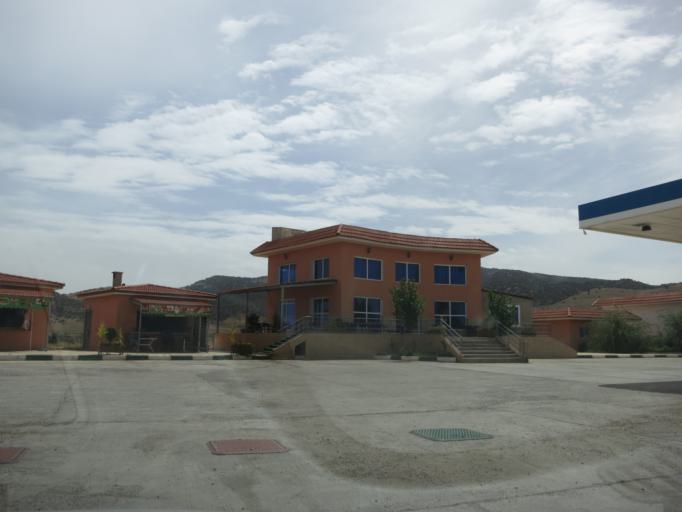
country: MA
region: Meknes-Tafilalet
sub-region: Ifrane
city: Azrou
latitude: 33.2220
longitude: -5.0597
